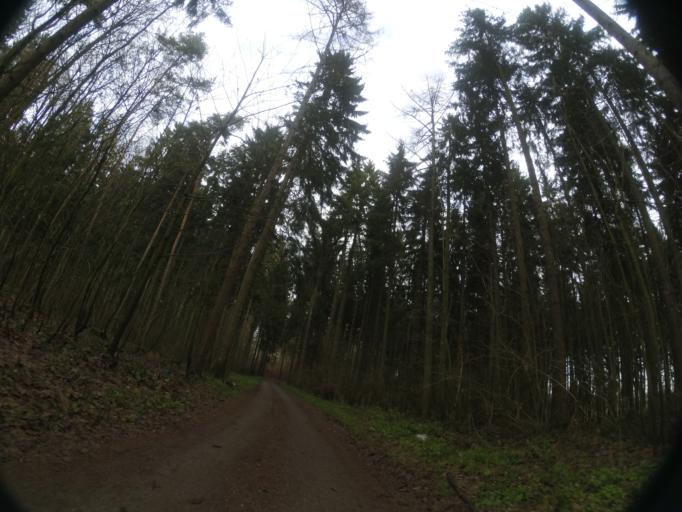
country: DE
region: Baden-Wuerttemberg
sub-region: Tuebingen Region
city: Erbach
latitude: 48.3642
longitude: 9.9262
